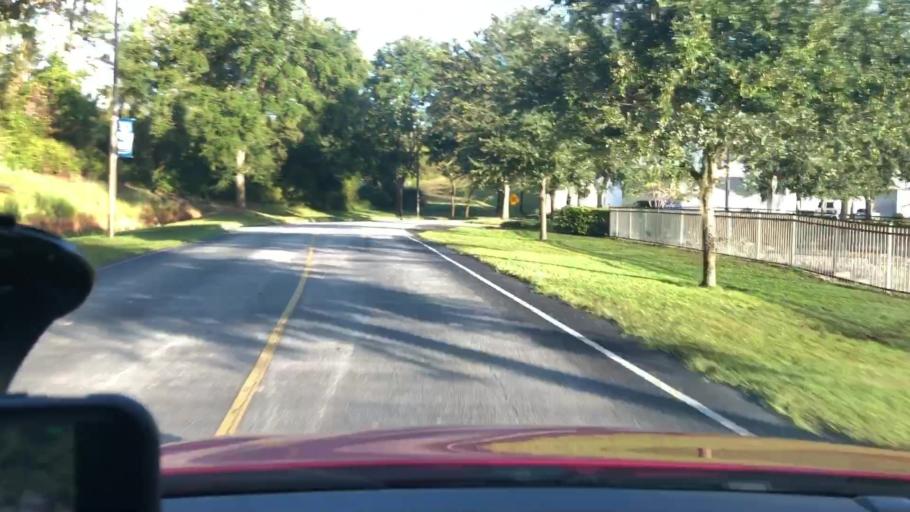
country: US
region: Florida
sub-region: Volusia County
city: Deltona
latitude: 28.9129
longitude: -81.2859
